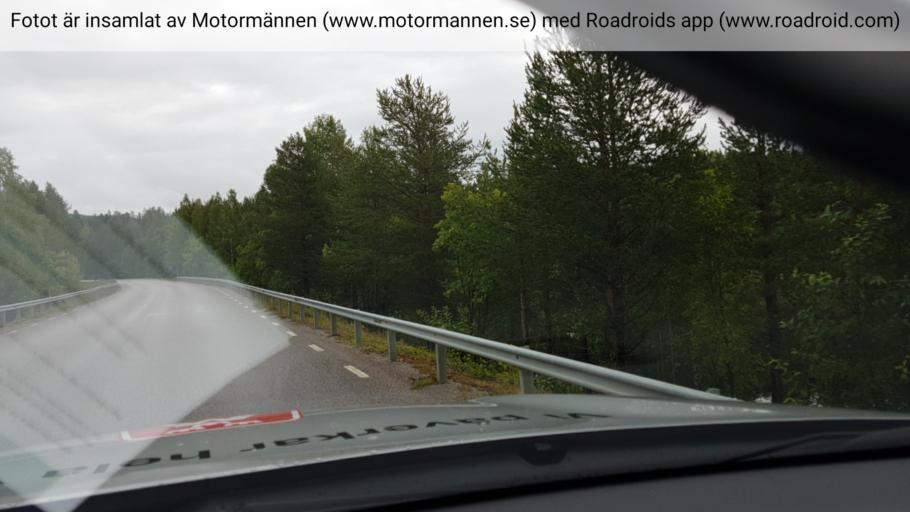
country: SE
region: Norrbotten
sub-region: Gallivare Kommun
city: Gaellivare
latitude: 66.4423
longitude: 20.6441
